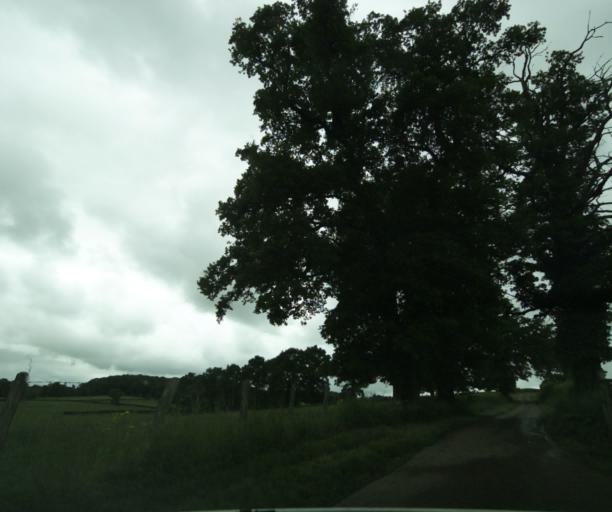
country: FR
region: Bourgogne
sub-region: Departement de Saone-et-Loire
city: Charolles
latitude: 46.4614
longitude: 4.2906
